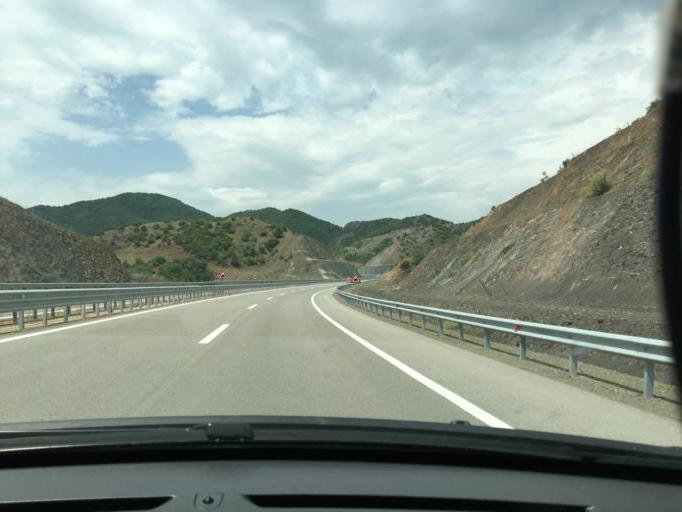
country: MK
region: Demir Kapija
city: Demir Kapija
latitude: 41.3711
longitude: 22.3331
